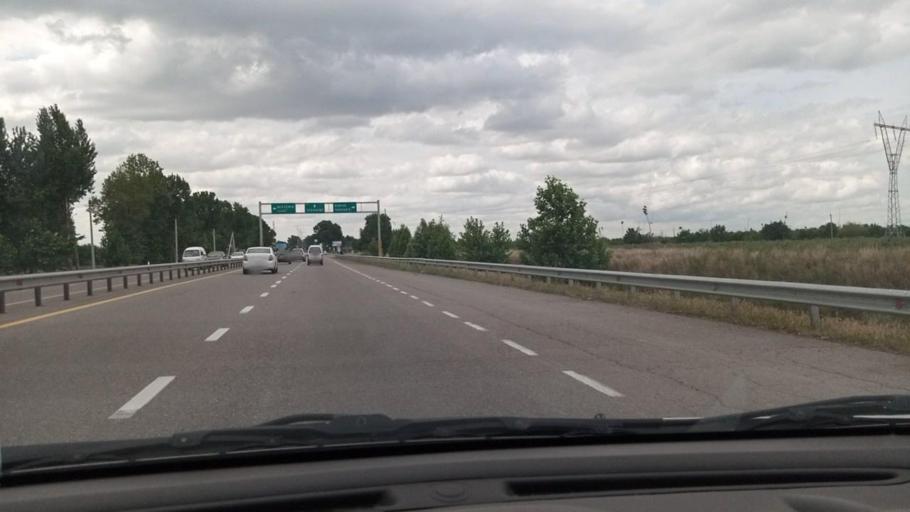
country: UZ
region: Toshkent Shahri
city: Bektemir
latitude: 41.1788
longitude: 69.4084
